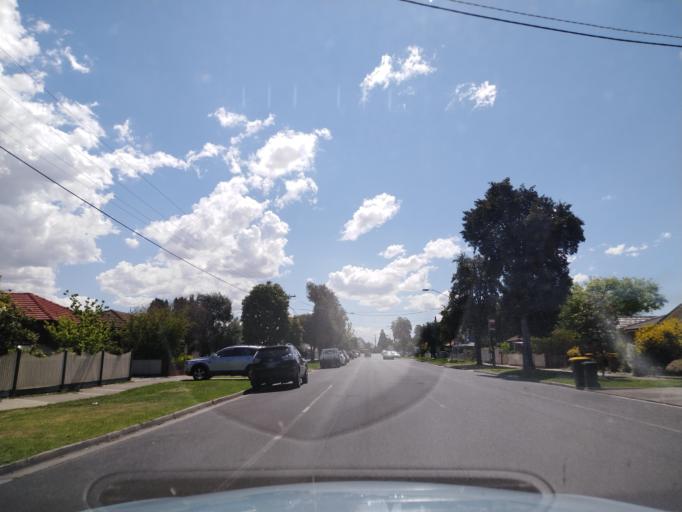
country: AU
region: Victoria
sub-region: Hobsons Bay
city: South Kingsville
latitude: -37.8347
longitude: 144.8622
